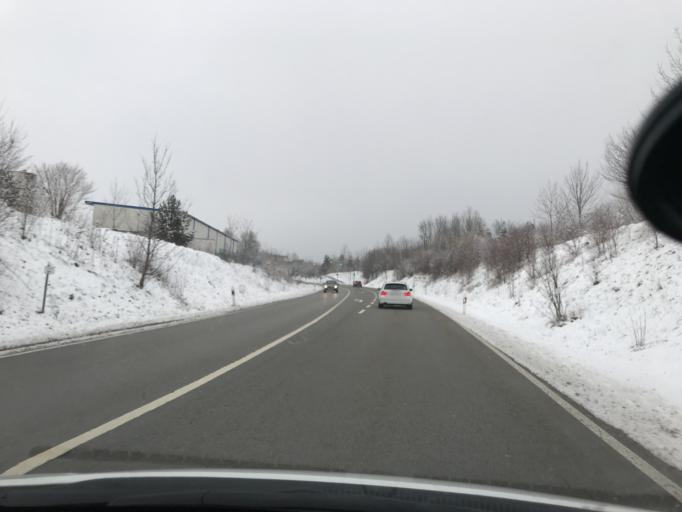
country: DE
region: Bavaria
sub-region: Upper Bavaria
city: Neubiberg
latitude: 48.0684
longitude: 11.6509
